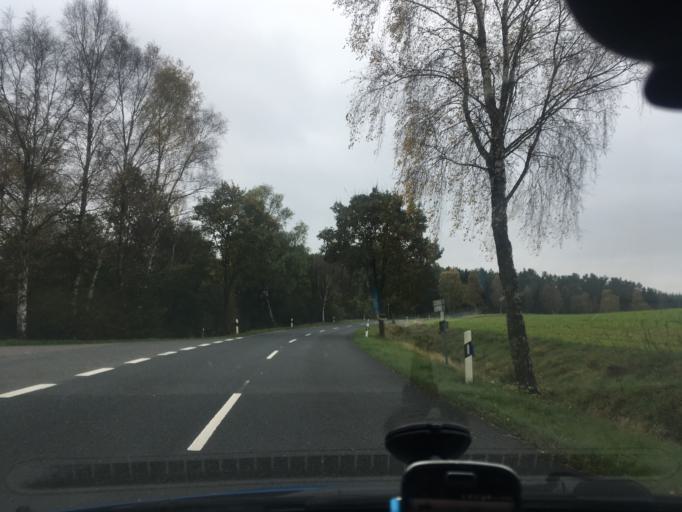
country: DE
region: Lower Saxony
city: Soderstorf
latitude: 53.1089
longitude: 10.0805
